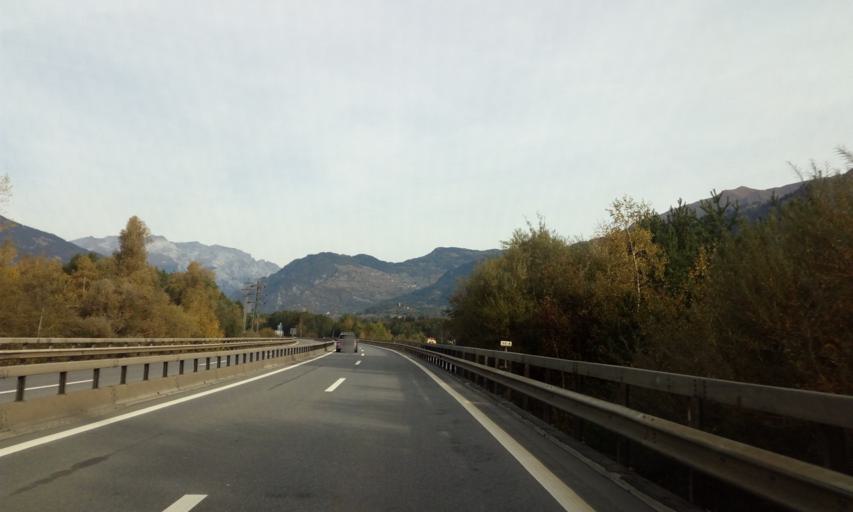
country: CH
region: Grisons
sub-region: Hinterrhein District
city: Thusis
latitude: 46.7074
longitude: 9.4490
